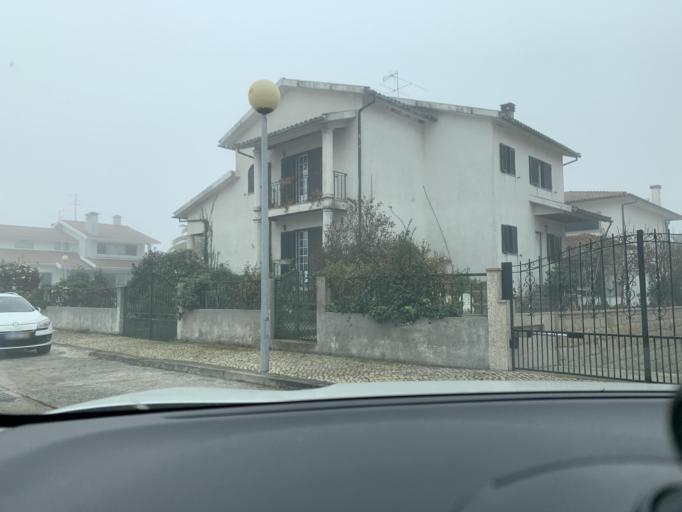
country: PT
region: Viseu
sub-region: Viseu
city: Rio de Loba
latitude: 40.6399
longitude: -7.8640
